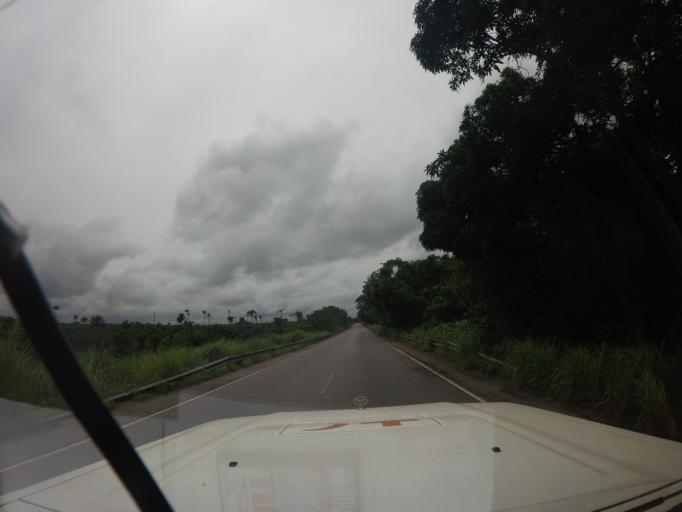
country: SL
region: Northern Province
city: Magburaka
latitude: 8.7434
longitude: -11.9621
